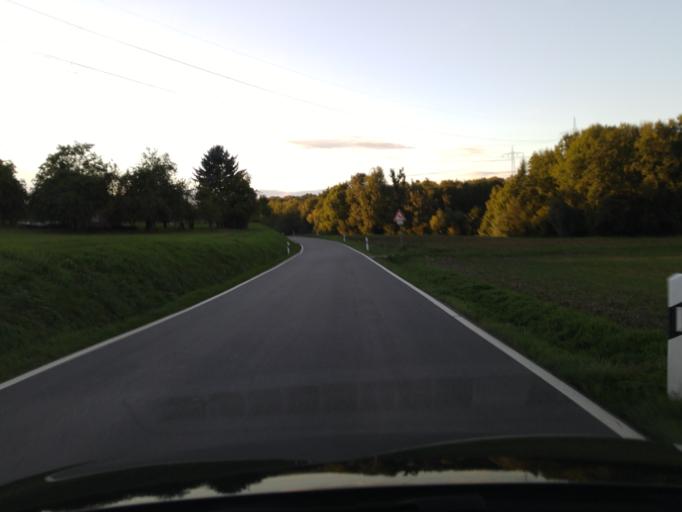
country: DE
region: Baden-Wuerttemberg
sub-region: Regierungsbezirk Stuttgart
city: Bad Wimpfen
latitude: 49.2003
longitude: 9.1356
